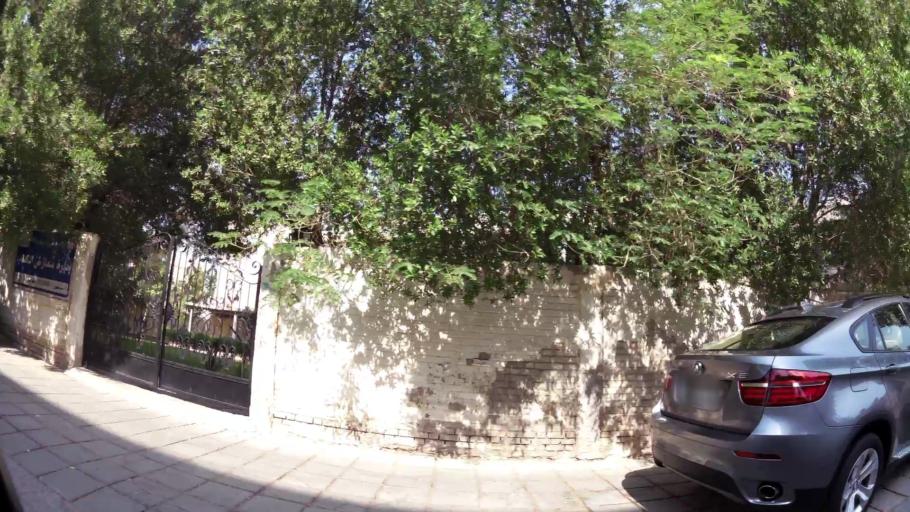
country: KW
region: Muhafazat Hawalli
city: Hawalli
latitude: 29.3467
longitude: 48.0272
